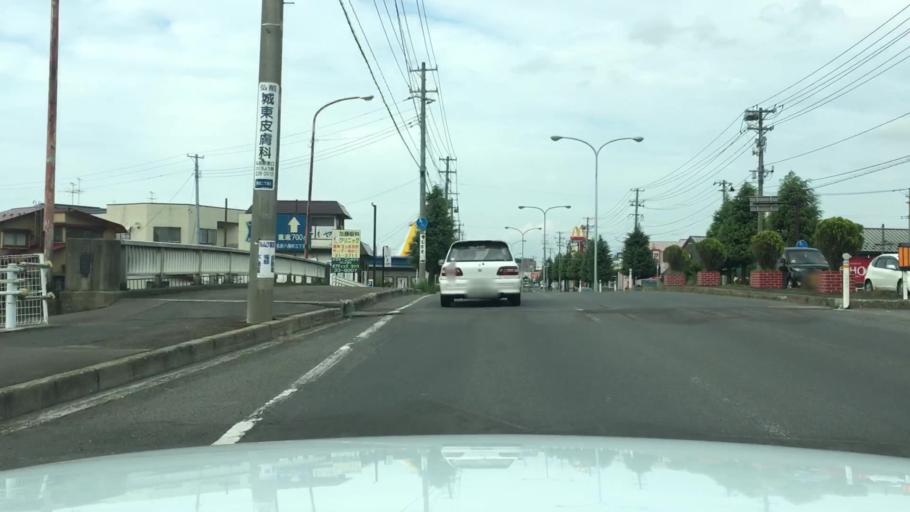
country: JP
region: Aomori
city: Hirosaki
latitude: 40.6103
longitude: 140.4815
